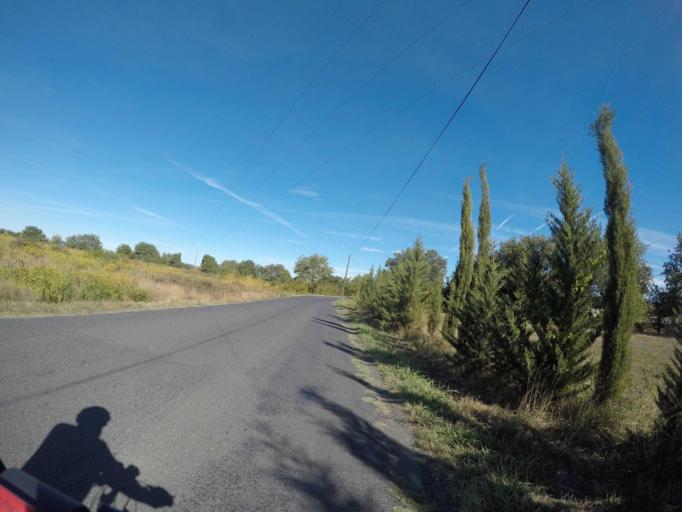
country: FR
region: Languedoc-Roussillon
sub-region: Departement des Pyrenees-Orientales
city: Ponteilla
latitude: 42.6430
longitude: 2.8024
